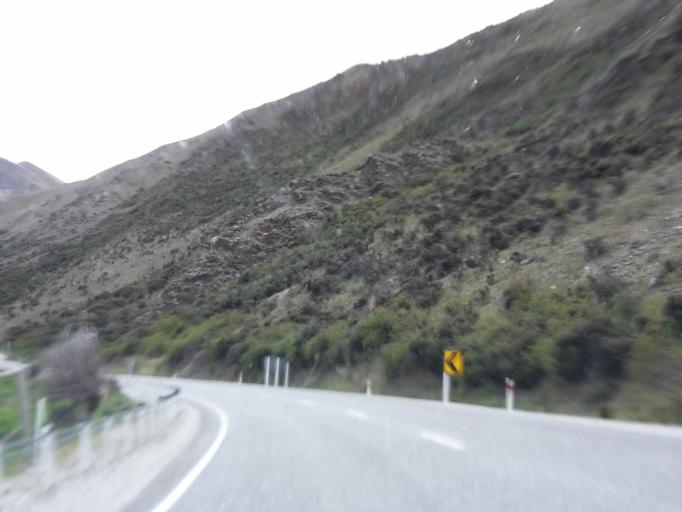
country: NZ
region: Otago
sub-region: Queenstown-Lakes District
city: Wanaka
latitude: -44.6006
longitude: 169.5648
